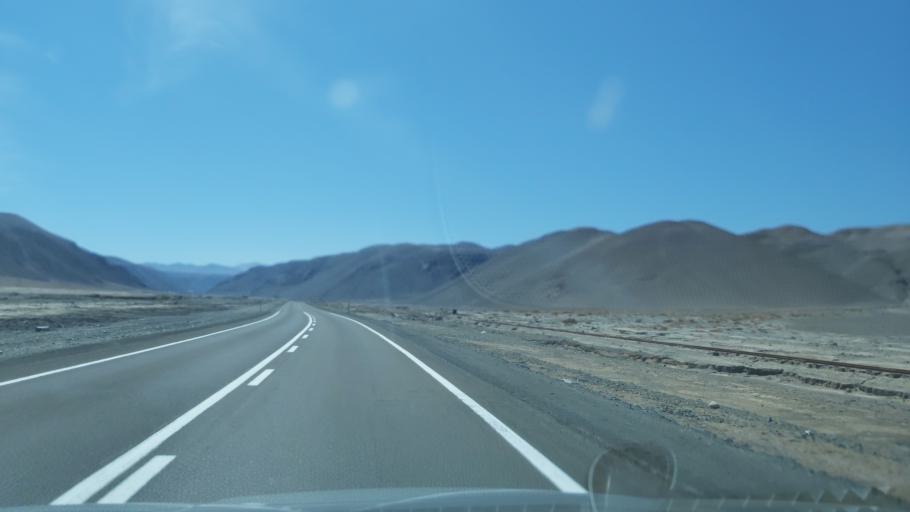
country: CL
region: Atacama
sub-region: Provincia de Chanaral
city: Diego de Almagro
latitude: -26.3489
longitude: -69.8636
